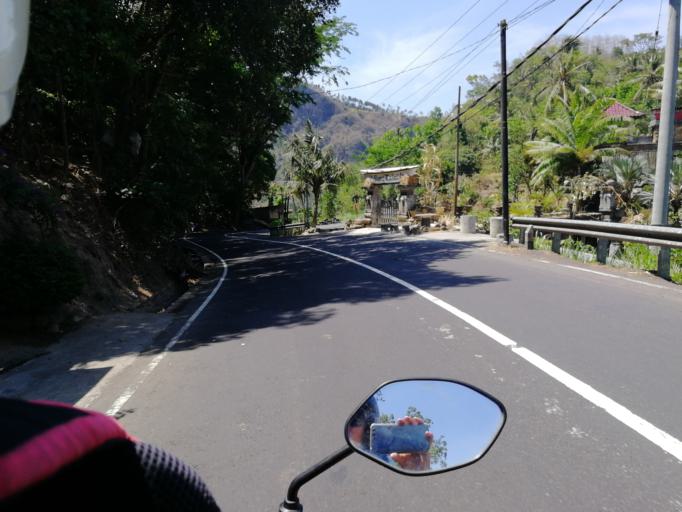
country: ID
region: Bali
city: Tistagede
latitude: -8.3720
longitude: 115.6099
